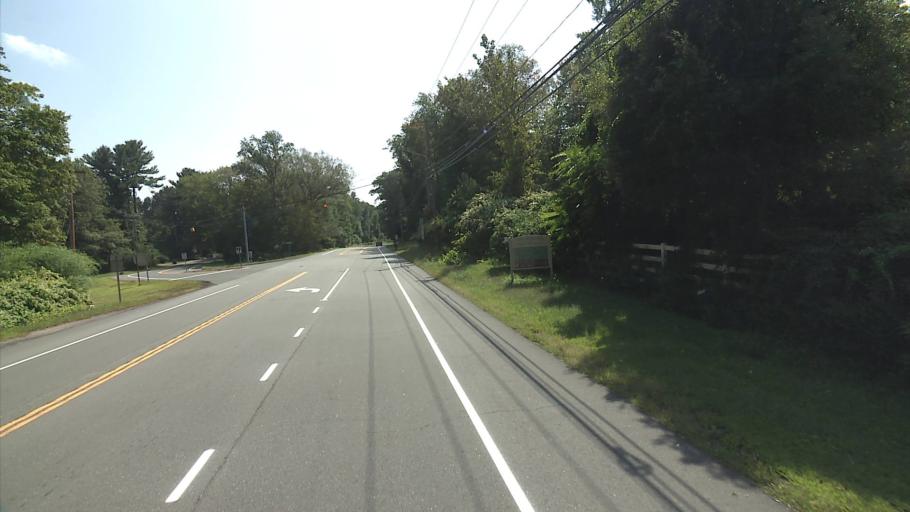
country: US
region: Connecticut
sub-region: New Haven County
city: Madison Center
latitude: 41.3227
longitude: -72.6122
